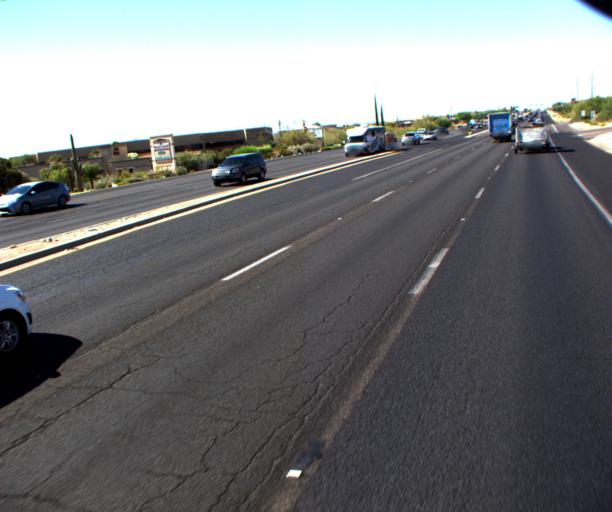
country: US
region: Arizona
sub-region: Pima County
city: Casas Adobes
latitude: 32.3414
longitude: -110.9769
